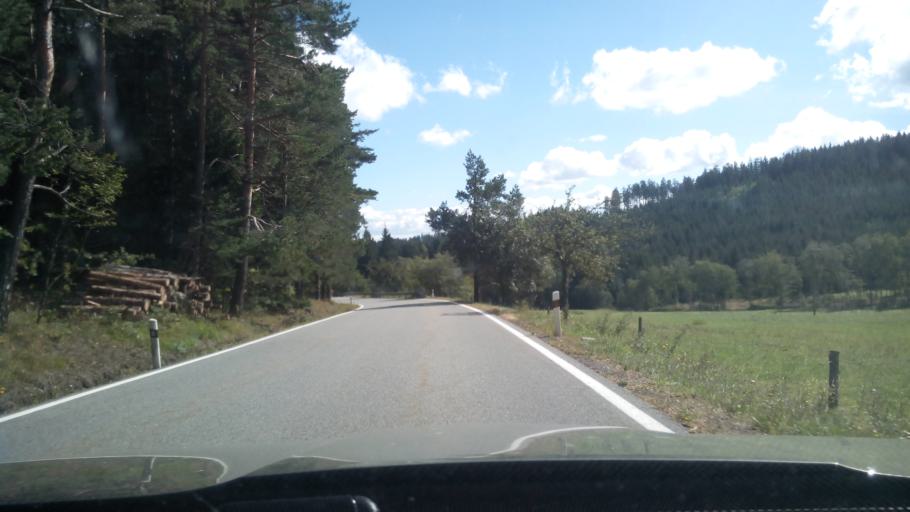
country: CZ
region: Jihocesky
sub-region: Okres Prachatice
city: Stachy
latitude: 49.1210
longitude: 13.6255
